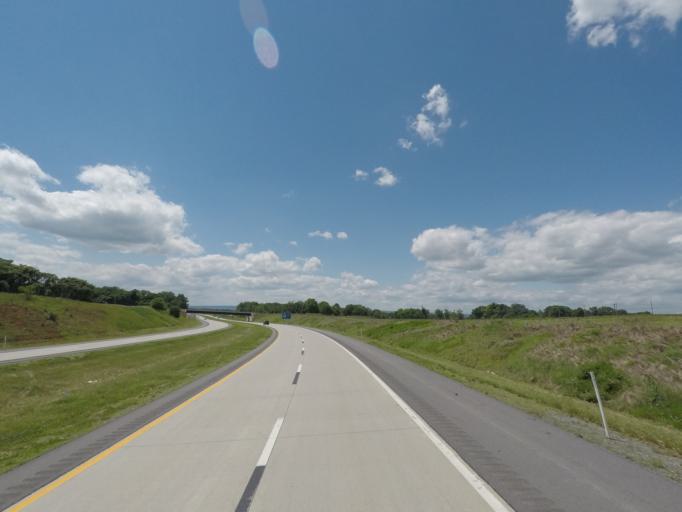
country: US
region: West Virginia
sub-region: Berkeley County
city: Martinsburg
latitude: 39.3938
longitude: -77.8966
